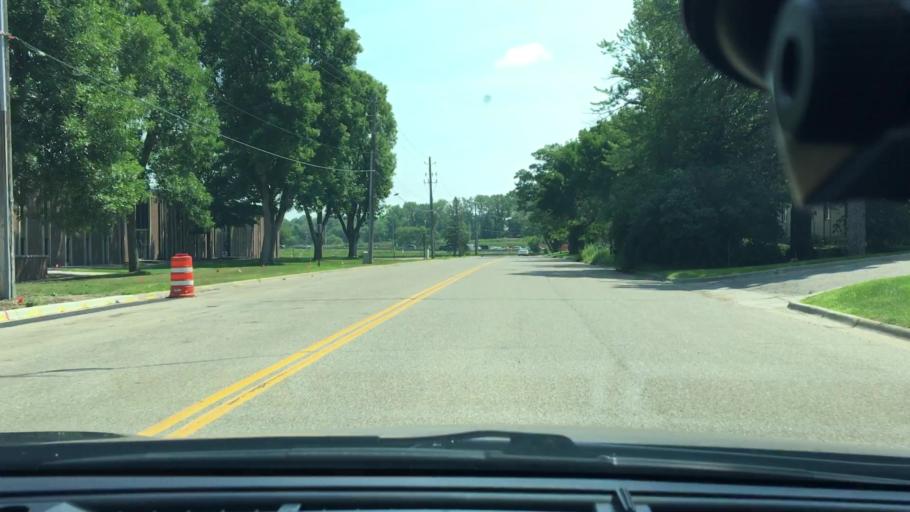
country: US
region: Minnesota
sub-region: Hennepin County
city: New Hope
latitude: 44.9894
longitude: -93.4039
